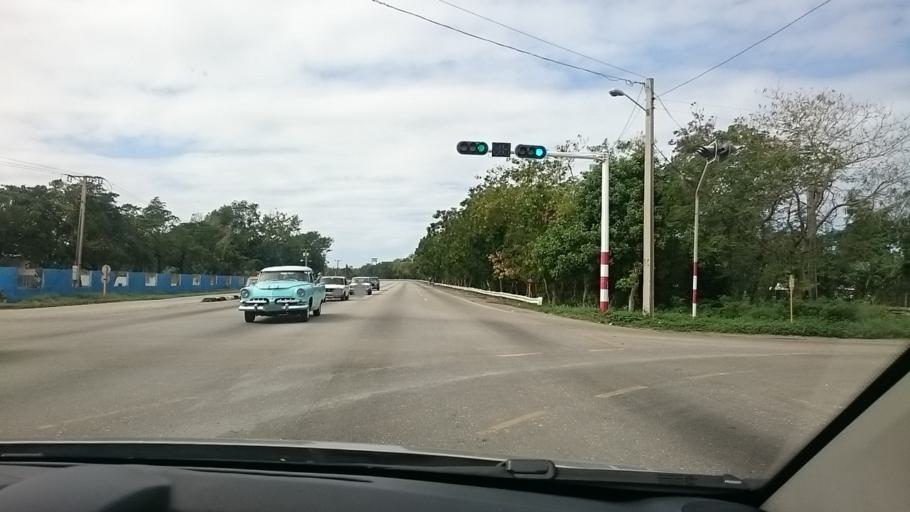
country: CU
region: La Habana
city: Alamar
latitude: 23.1687
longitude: -82.2531
